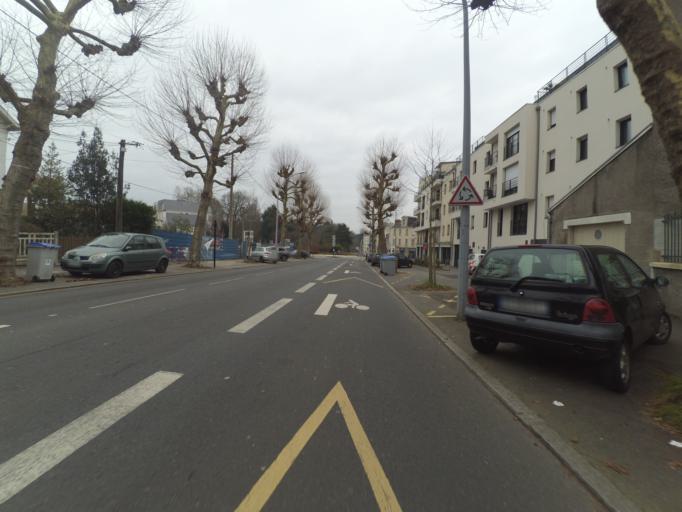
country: FR
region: Pays de la Loire
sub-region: Departement de la Loire-Atlantique
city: Nantes
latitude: 47.2221
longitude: -1.5866
